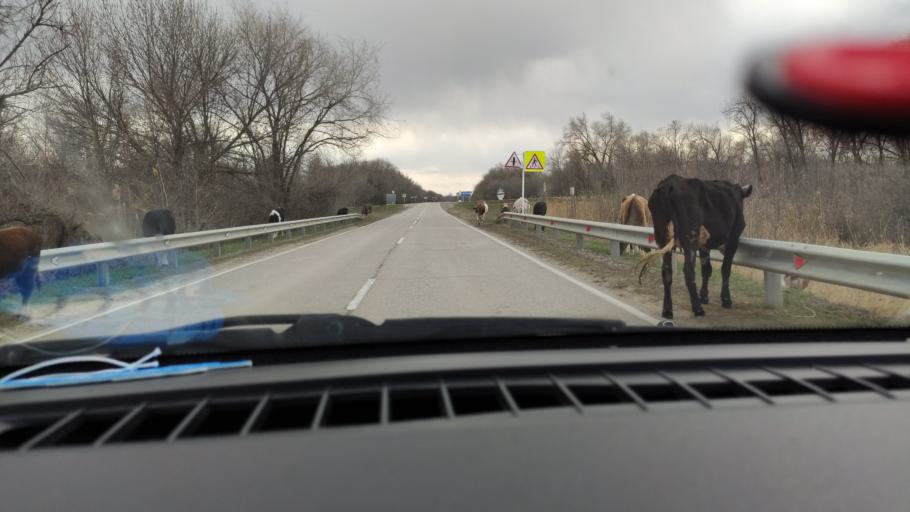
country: RU
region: Saratov
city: Privolzhskiy
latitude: 51.2480
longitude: 45.9368
